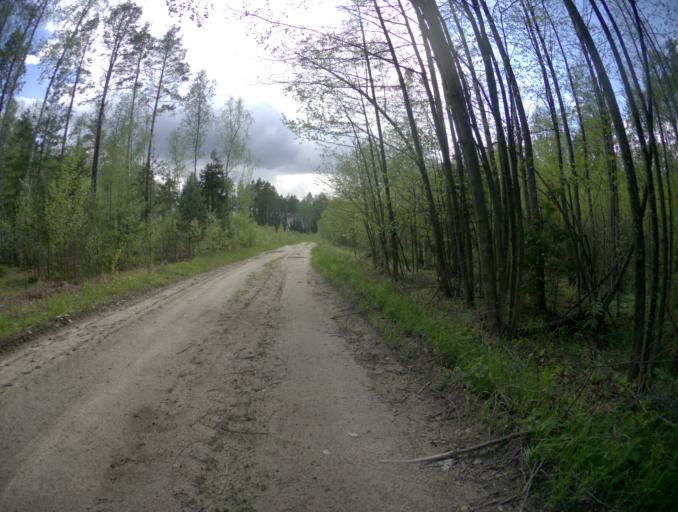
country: RU
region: Rjazan
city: Tuma
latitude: 55.2125
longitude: 40.4511
